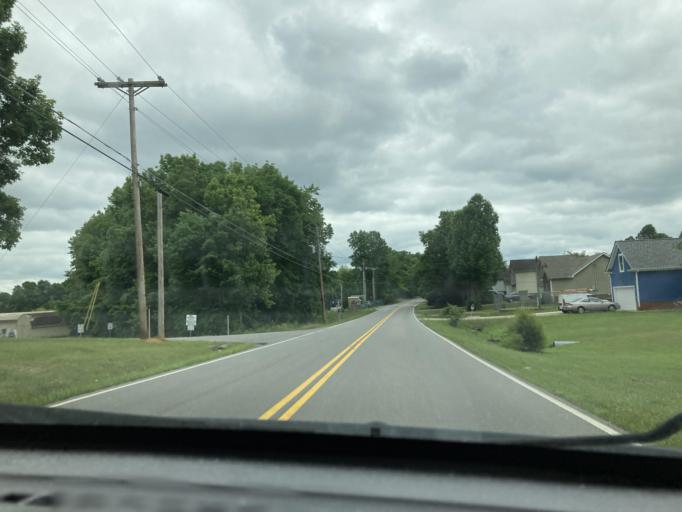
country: US
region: Tennessee
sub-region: Dickson County
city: Dickson
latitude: 36.0504
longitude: -87.3679
